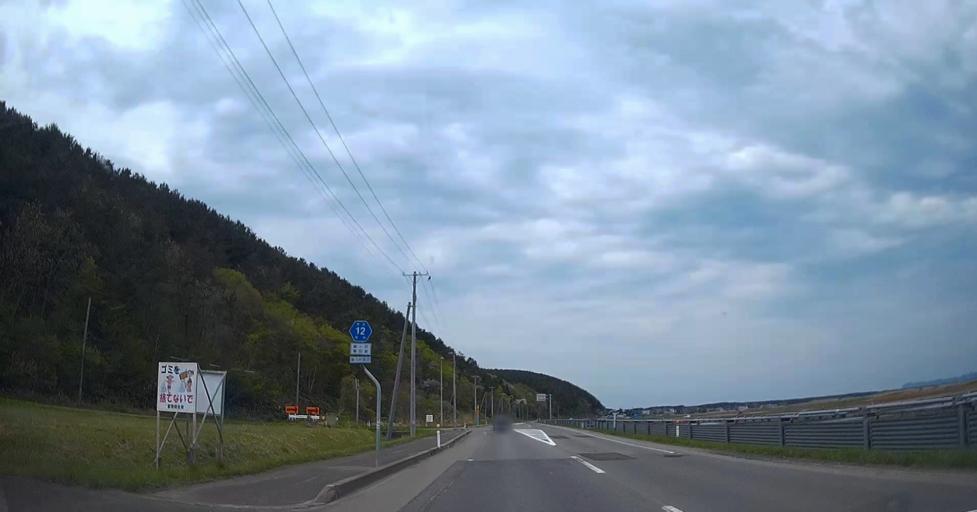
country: JP
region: Aomori
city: Shimokizukuri
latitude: 40.9948
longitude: 140.3541
